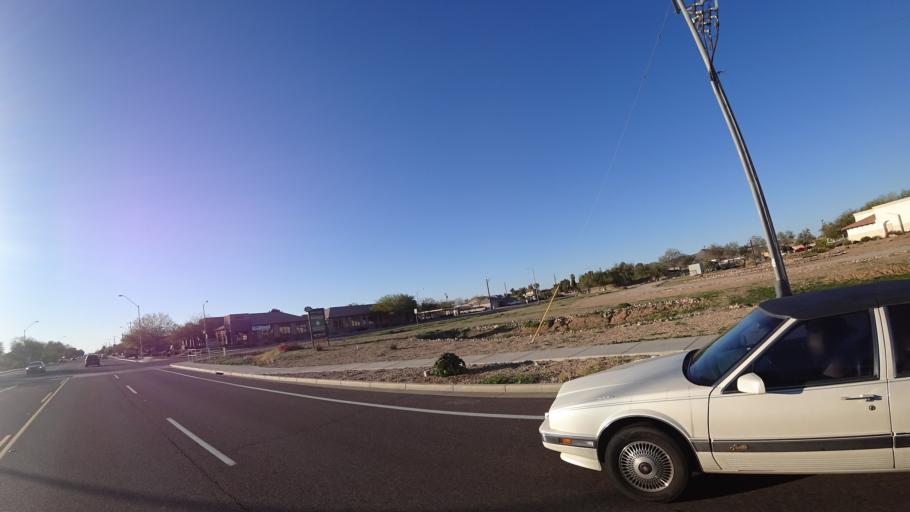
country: US
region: Arizona
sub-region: Maricopa County
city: Sun City
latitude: 33.6816
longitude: -112.2414
